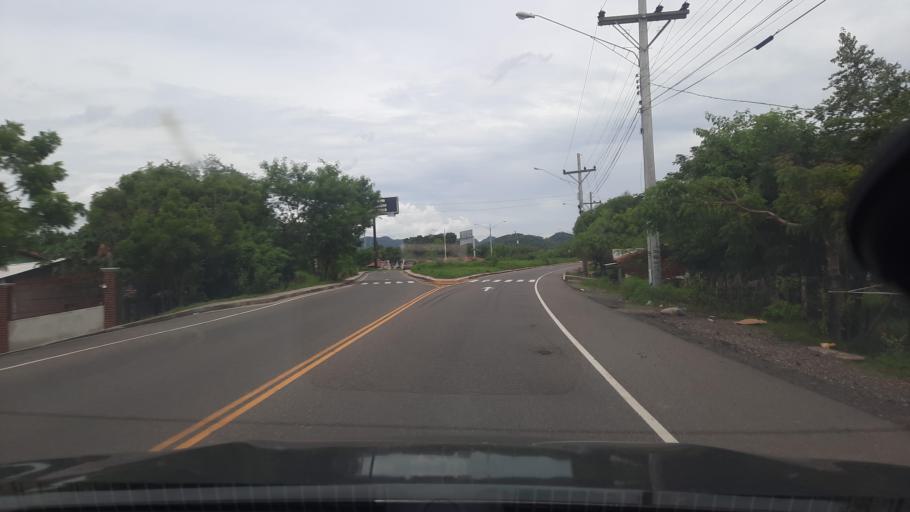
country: HN
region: Valle
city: Jicaro Galan
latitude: 13.5303
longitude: -87.4398
